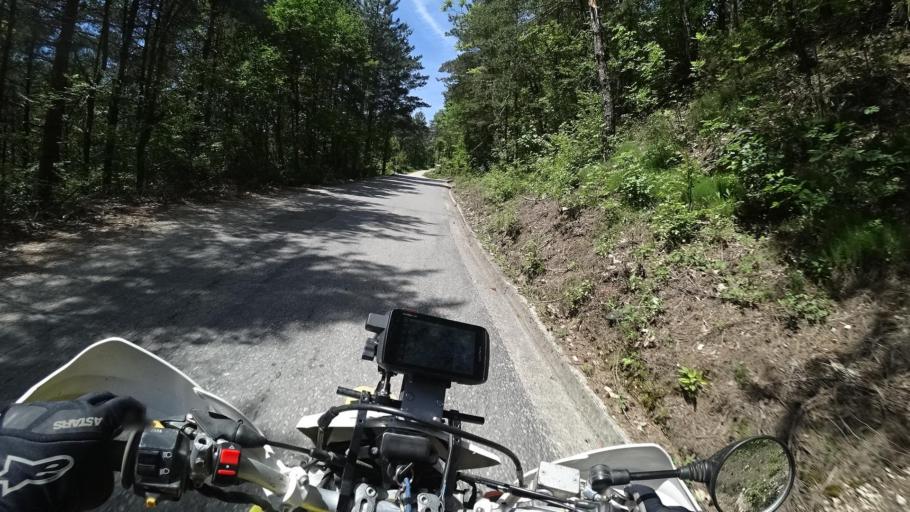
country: BA
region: Federation of Bosnia and Herzegovina
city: Polje-Bijela
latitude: 43.6204
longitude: 17.9797
